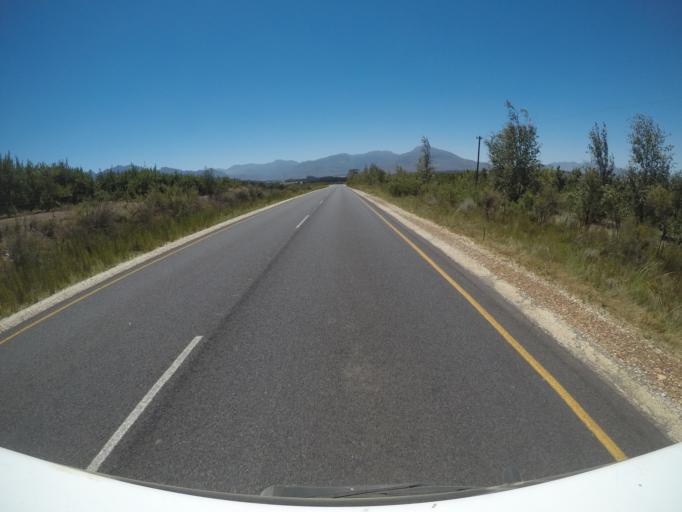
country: ZA
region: Western Cape
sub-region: Overberg District Municipality
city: Grabouw
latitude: -34.0634
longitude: 19.1345
